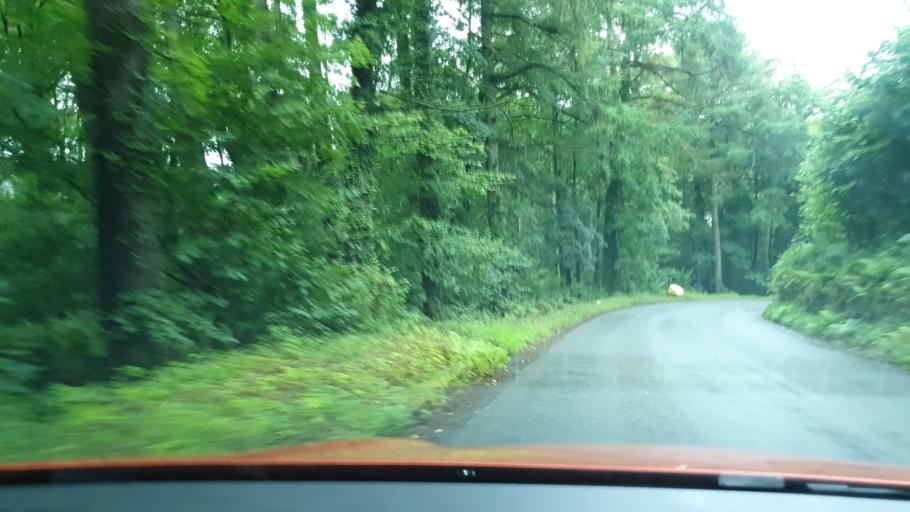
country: GB
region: England
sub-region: Cumbria
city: Seascale
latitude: 54.3922
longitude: -3.3411
